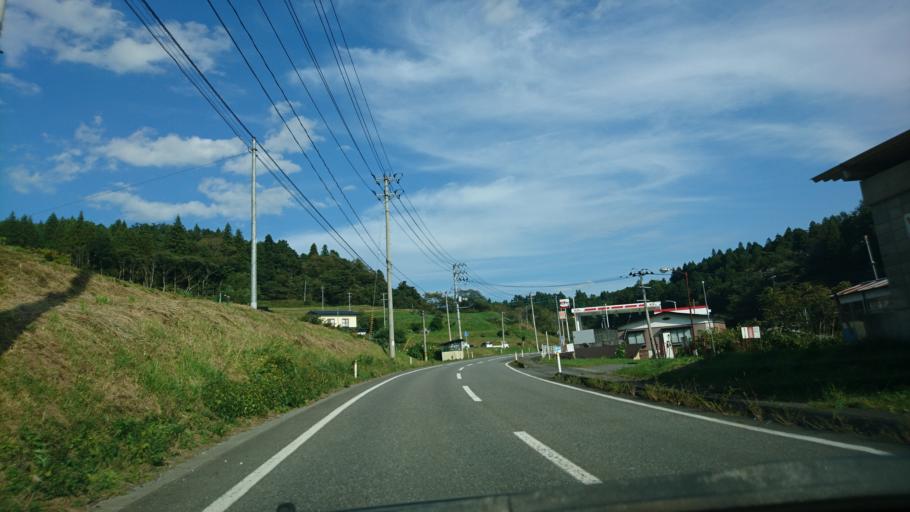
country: JP
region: Iwate
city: Ichinoseki
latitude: 38.8572
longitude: 141.3358
